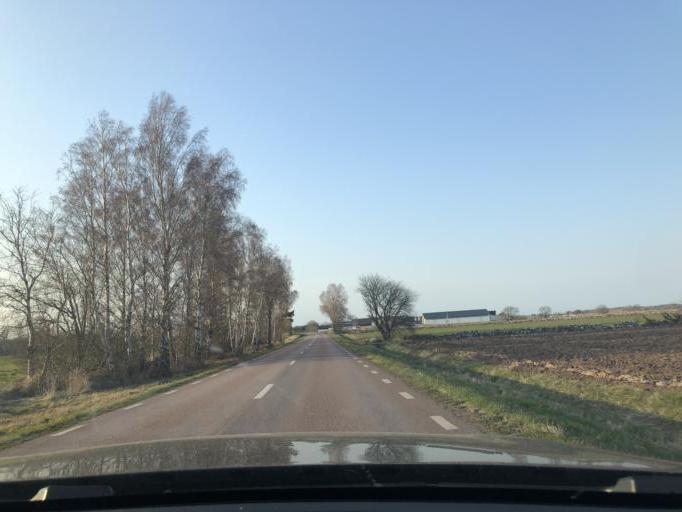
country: SE
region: Kalmar
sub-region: Morbylanga Kommun
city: Sodra Sandby
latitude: 56.5596
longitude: 16.6207
